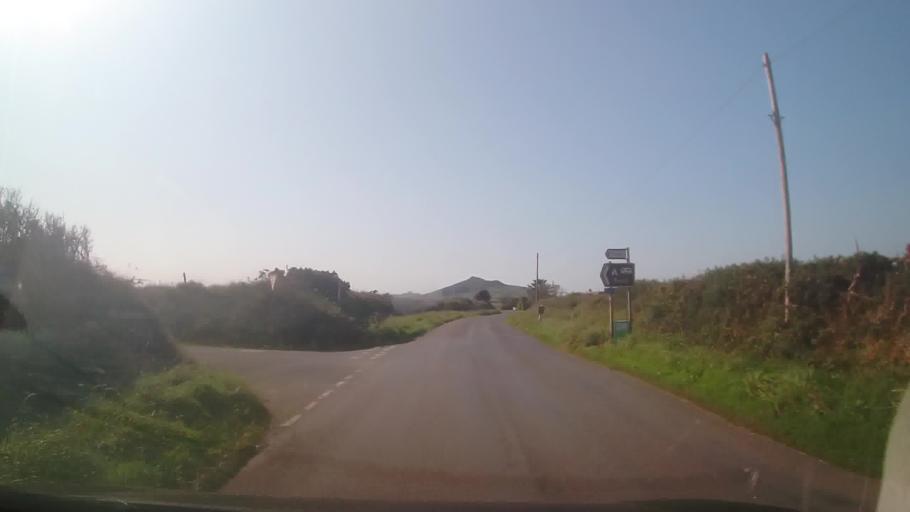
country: GB
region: Wales
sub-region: Pembrokeshire
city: Llanrhian
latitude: 51.9210
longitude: -5.2220
